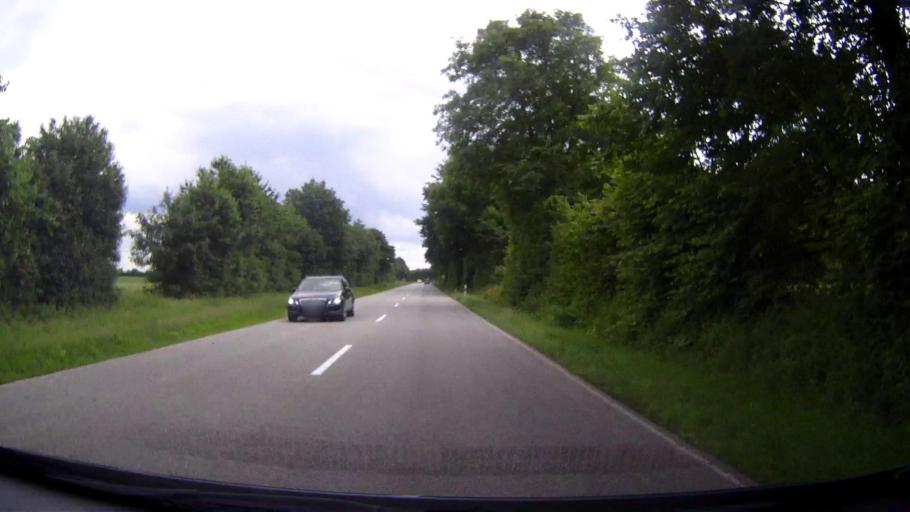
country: DE
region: Schleswig-Holstein
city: Seefeld
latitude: 54.1000
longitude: 9.4681
